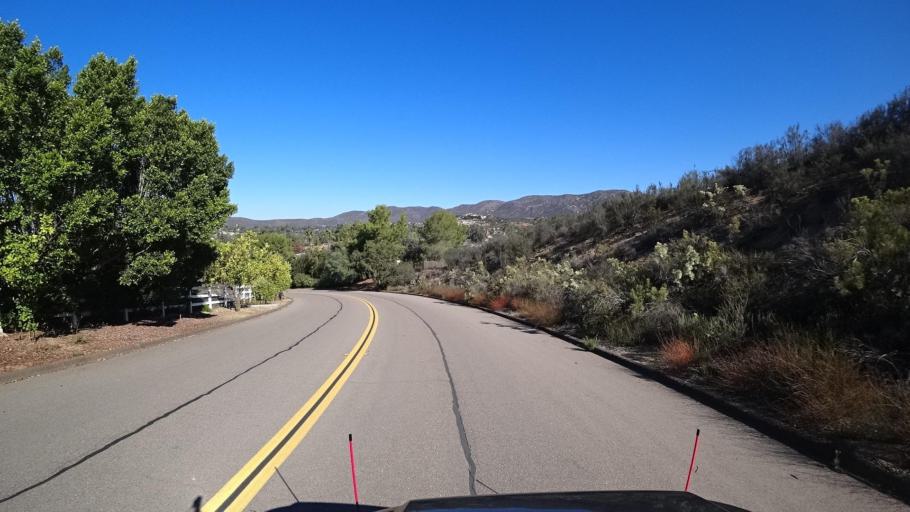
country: US
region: California
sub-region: San Diego County
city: Jamul
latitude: 32.7164
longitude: -116.8479
